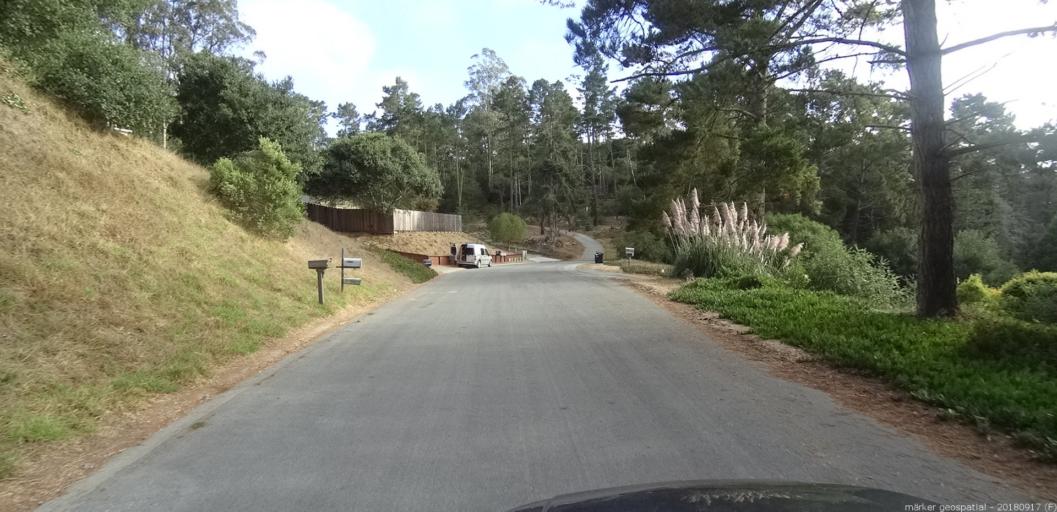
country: US
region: California
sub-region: Monterey County
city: Elkhorn
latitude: 36.8147
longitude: -121.7053
